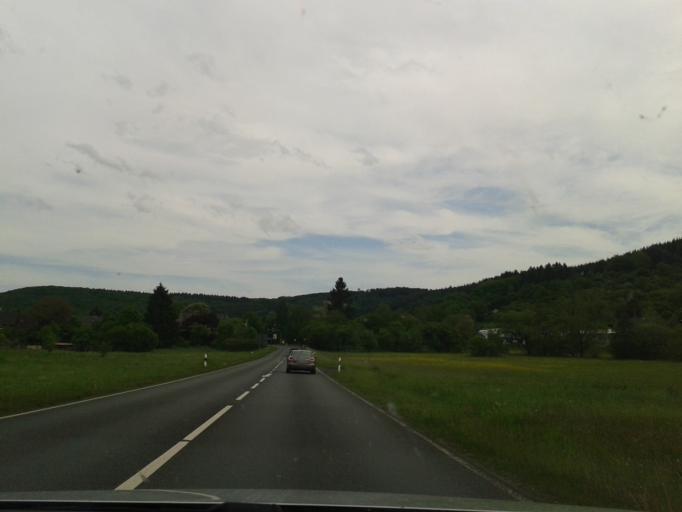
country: DE
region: Hesse
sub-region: Regierungsbezirk Giessen
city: Mittenaar
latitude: 50.6978
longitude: 8.4112
